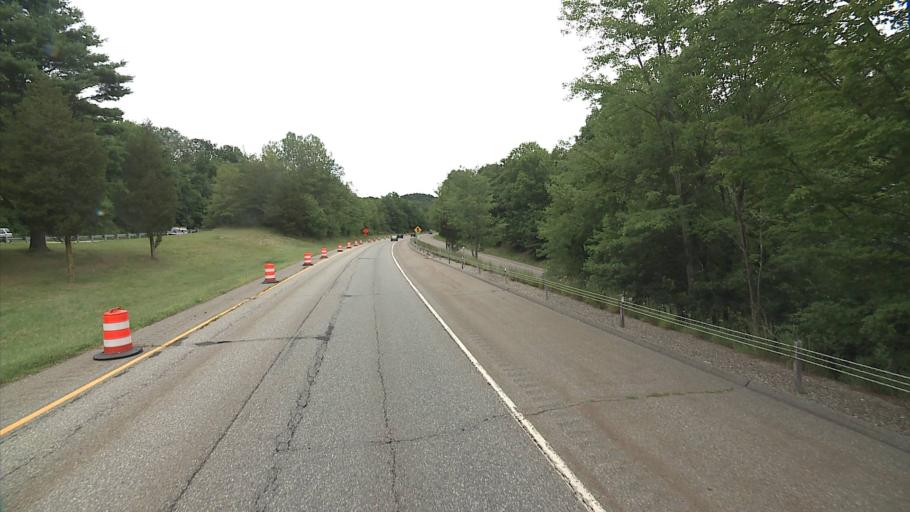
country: US
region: Connecticut
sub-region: Litchfield County
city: Northwest Harwinton
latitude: 41.7276
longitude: -73.1031
